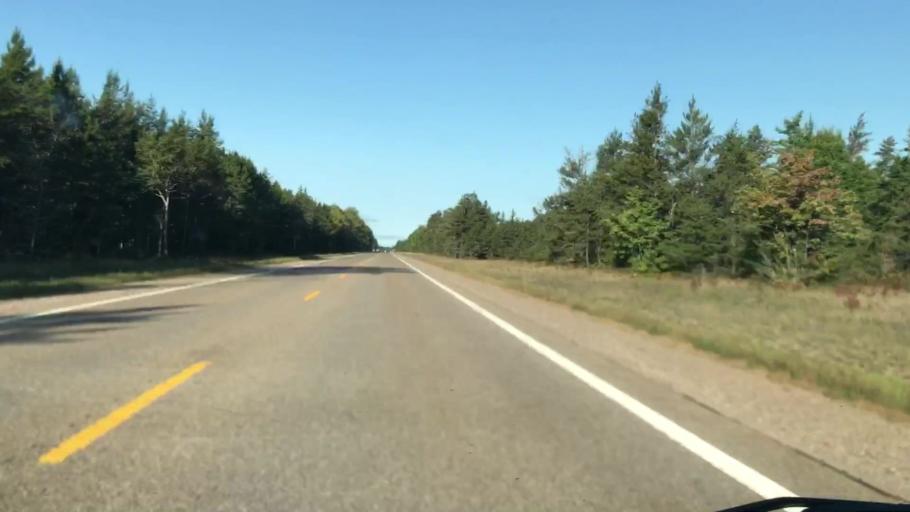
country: US
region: Michigan
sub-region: Mackinac County
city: Saint Ignace
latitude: 46.3585
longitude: -84.8502
